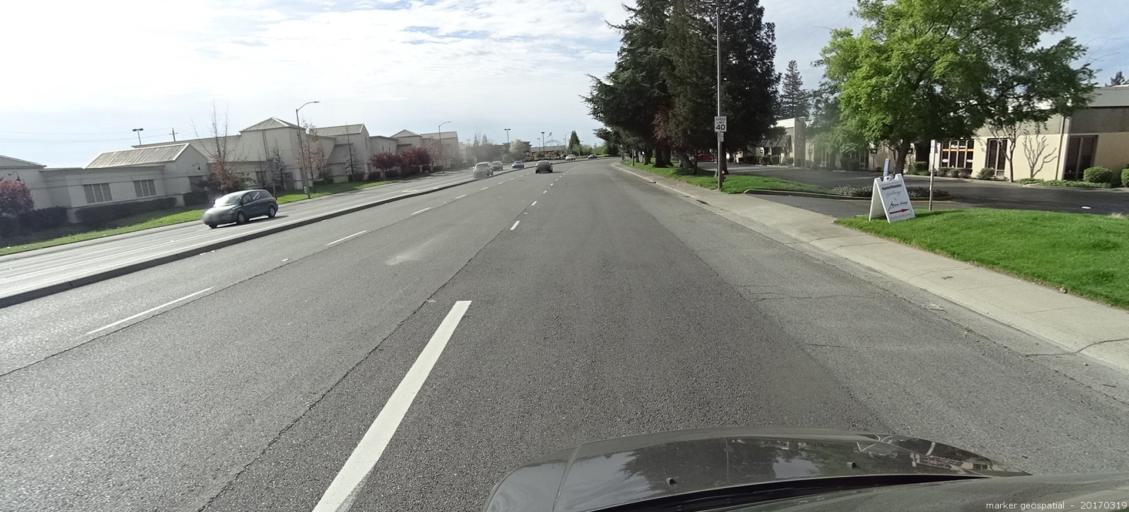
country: US
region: California
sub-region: Sacramento County
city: Rio Linda
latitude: 38.6471
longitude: -121.4755
